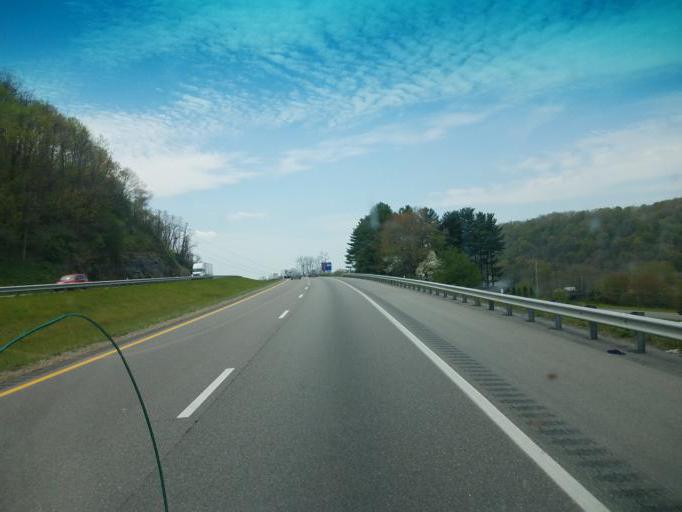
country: US
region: Virginia
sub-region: Smyth County
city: Atkins
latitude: 36.8622
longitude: -81.4457
